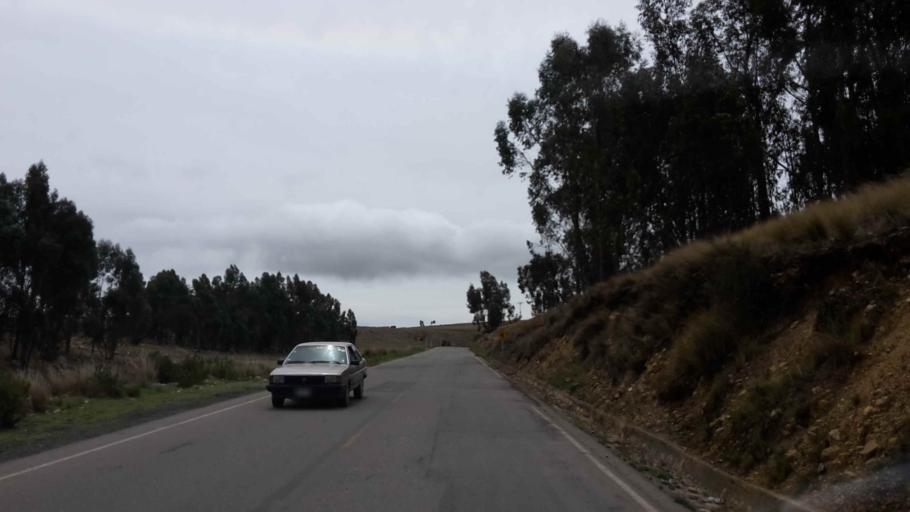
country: BO
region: Cochabamba
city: Arani
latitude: -17.4866
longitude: -65.6102
